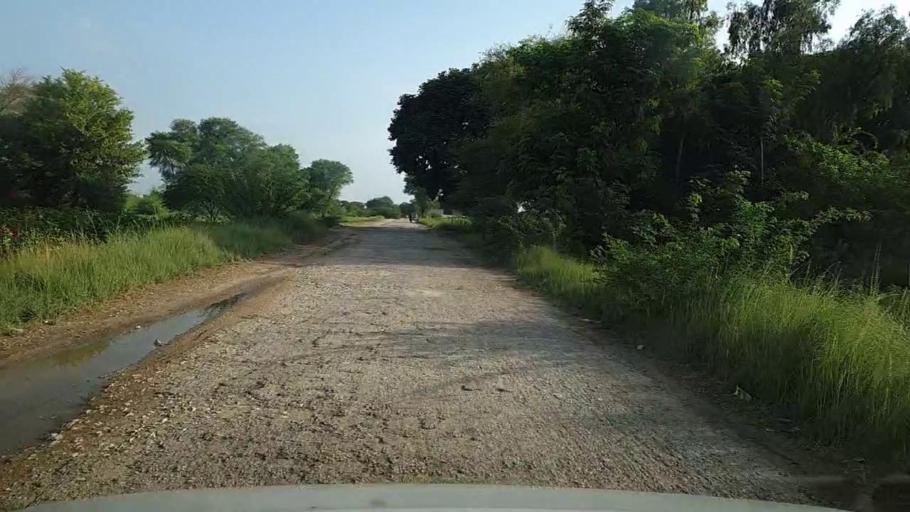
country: PK
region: Sindh
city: Pad Idan
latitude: 26.8002
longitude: 68.2360
